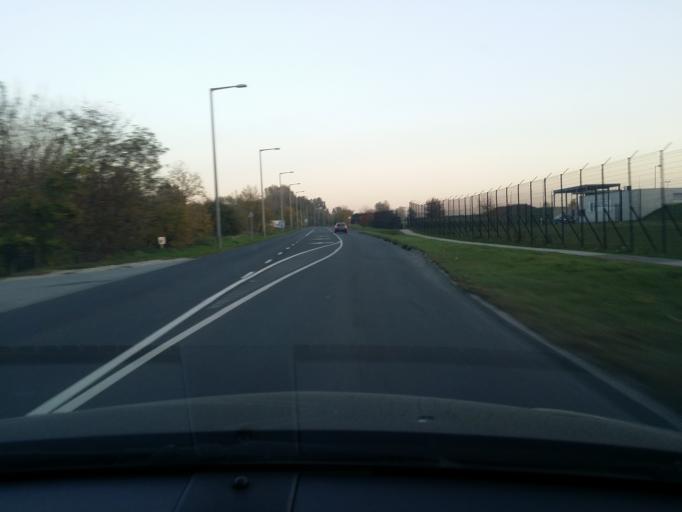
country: HU
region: Budapest
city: Budapest XV. keruelet
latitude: 47.5819
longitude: 19.1376
